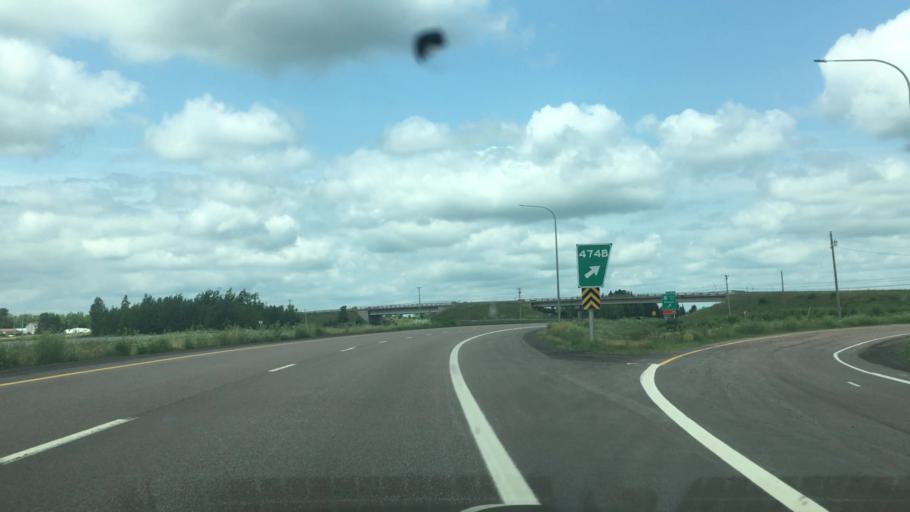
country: CA
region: New Brunswick
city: Dieppe
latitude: 46.0990
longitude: -64.6048
